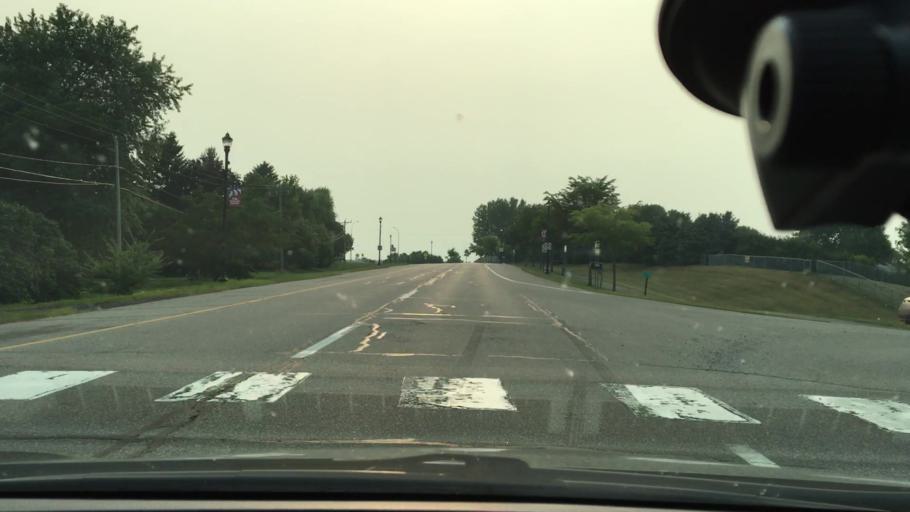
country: US
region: Minnesota
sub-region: Wright County
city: Saint Michael
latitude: 45.2102
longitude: -93.6702
